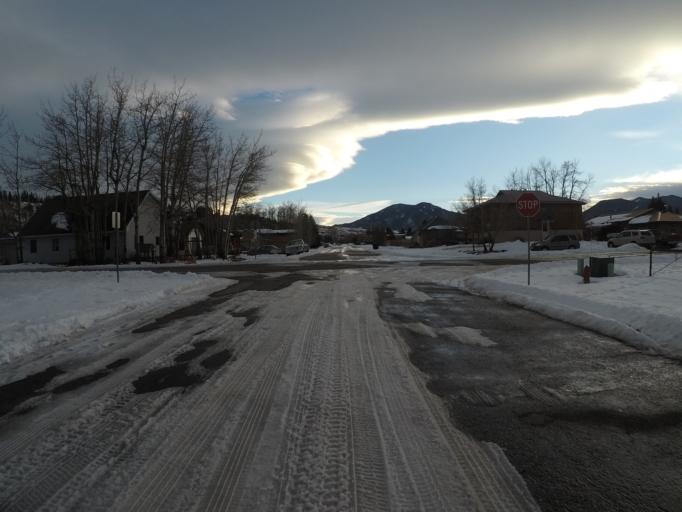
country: US
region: Montana
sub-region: Carbon County
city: Red Lodge
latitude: 45.1931
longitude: -109.2432
